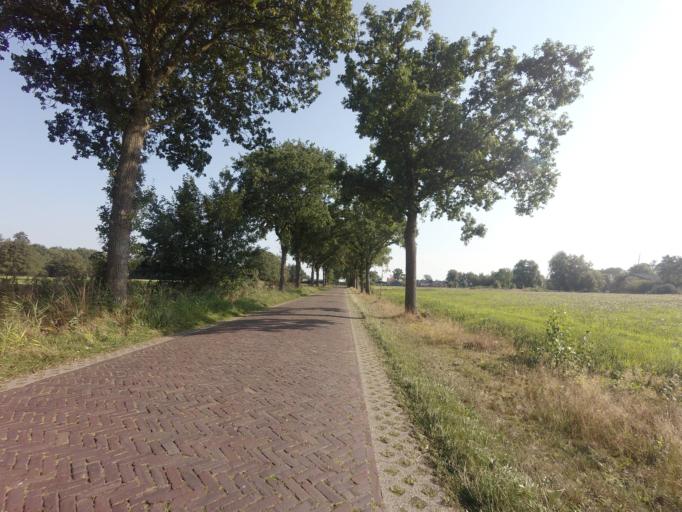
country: NL
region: Groningen
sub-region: Gemeente Zuidhorn
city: Aduard
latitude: 53.1714
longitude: 6.4769
